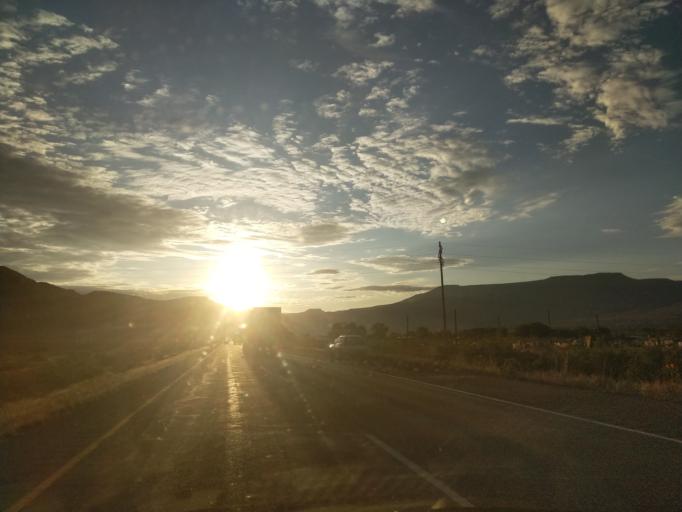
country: US
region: Colorado
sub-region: Mesa County
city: Clifton
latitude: 39.1084
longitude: -108.4259
